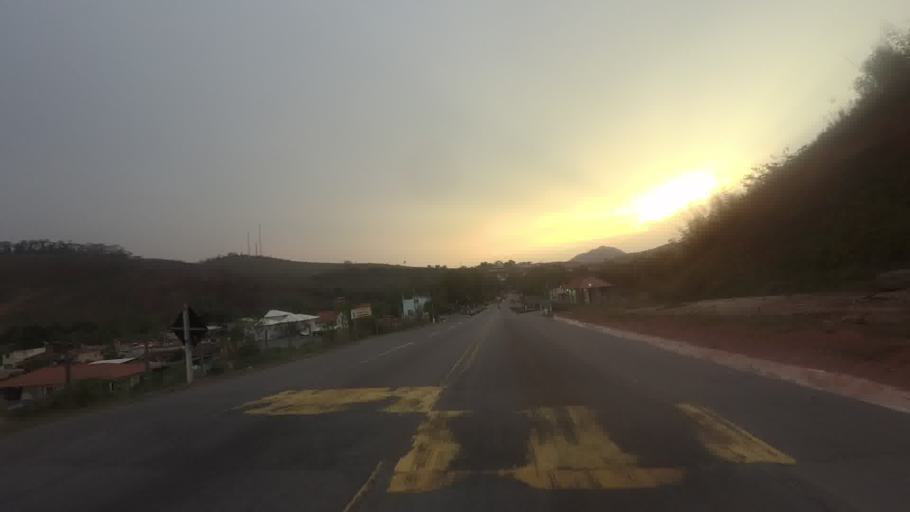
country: BR
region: Minas Gerais
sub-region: Recreio
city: Recreio
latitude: -21.7455
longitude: -42.4587
